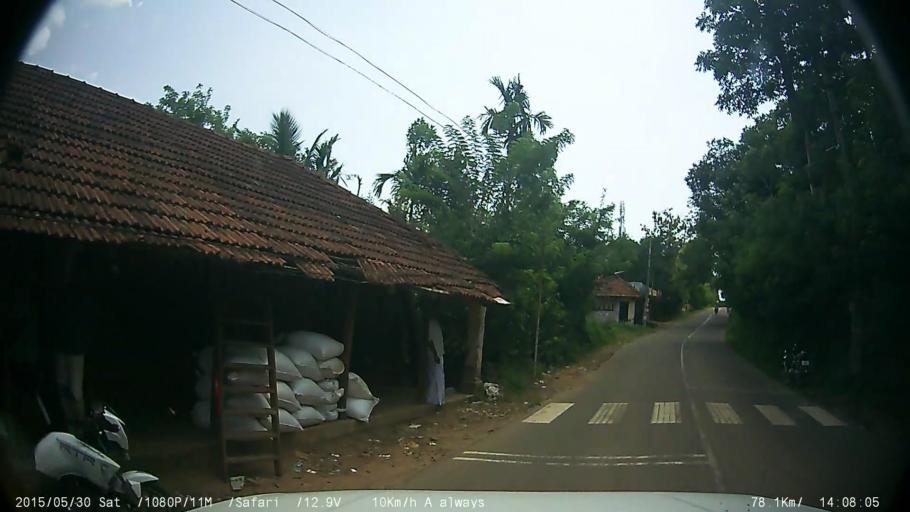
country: IN
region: Kerala
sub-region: Wayanad
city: Panamaram
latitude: 11.8105
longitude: 76.0557
